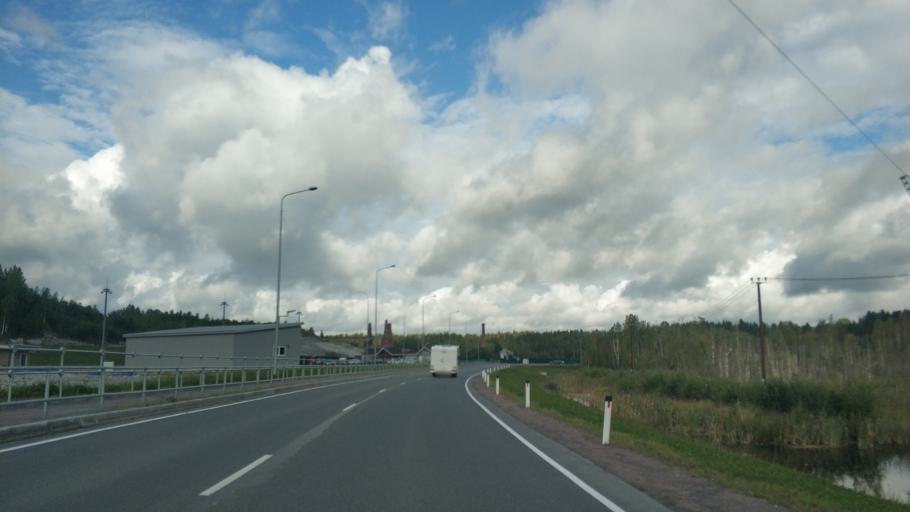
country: RU
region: Republic of Karelia
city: Ruskeala
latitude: 61.9480
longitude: 30.5883
